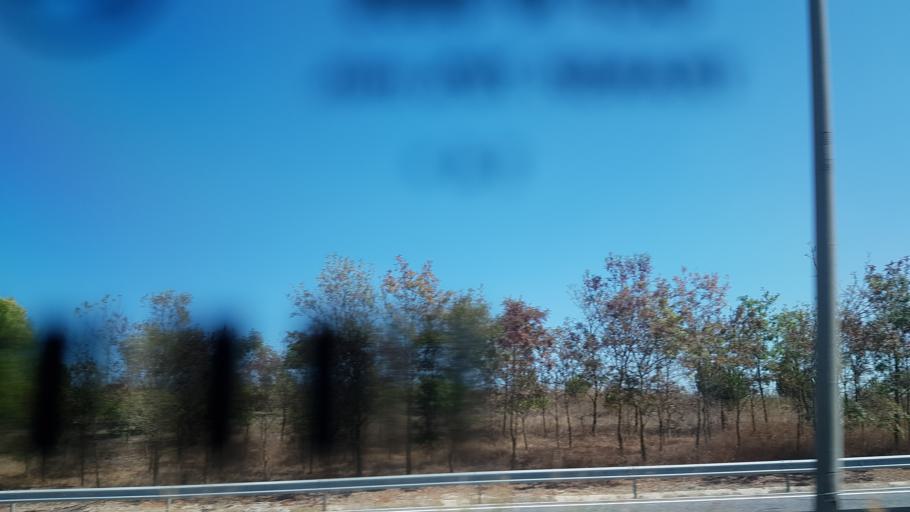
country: TR
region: Kirklareli
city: Luleburgaz
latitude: 41.4351
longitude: 27.3856
